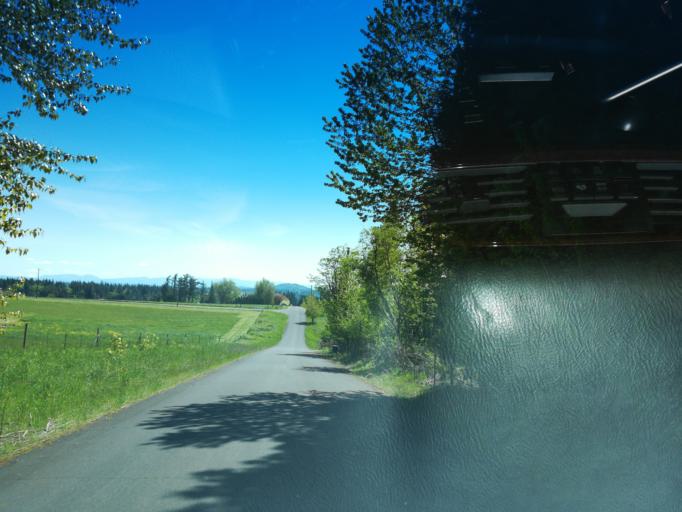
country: US
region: Oregon
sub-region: Multnomah County
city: Troutdale
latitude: 45.5352
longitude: -122.3623
